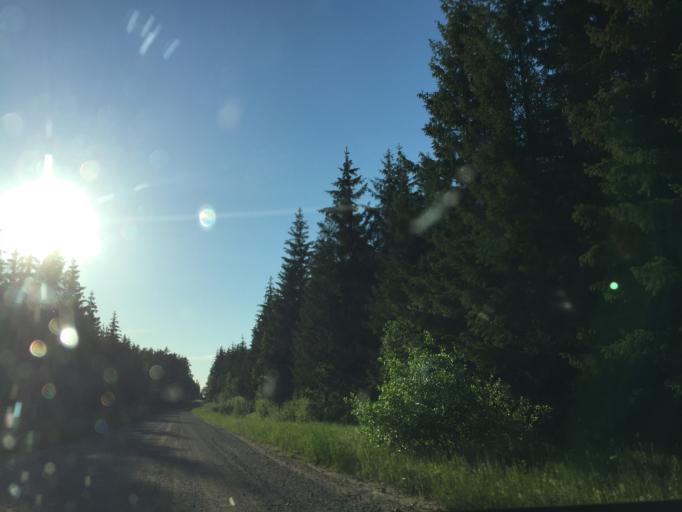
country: LV
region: Talsu Rajons
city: Sabile
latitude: 56.8710
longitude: 22.6296
